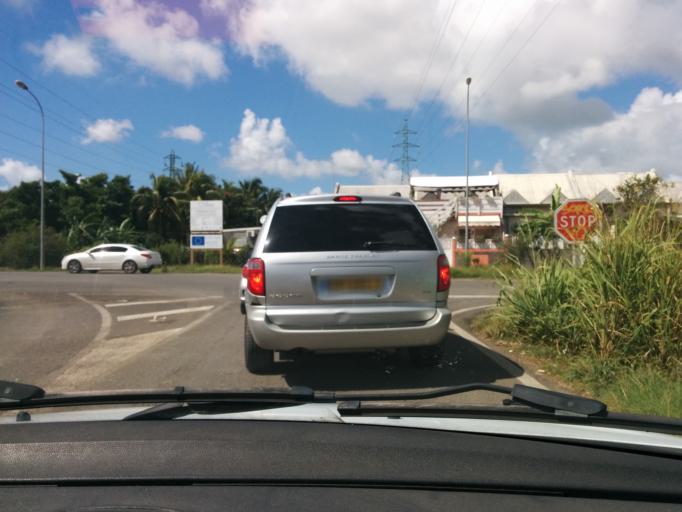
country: GP
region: Guadeloupe
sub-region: Guadeloupe
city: Pointe-a-Pitre
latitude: 16.2550
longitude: -61.5332
